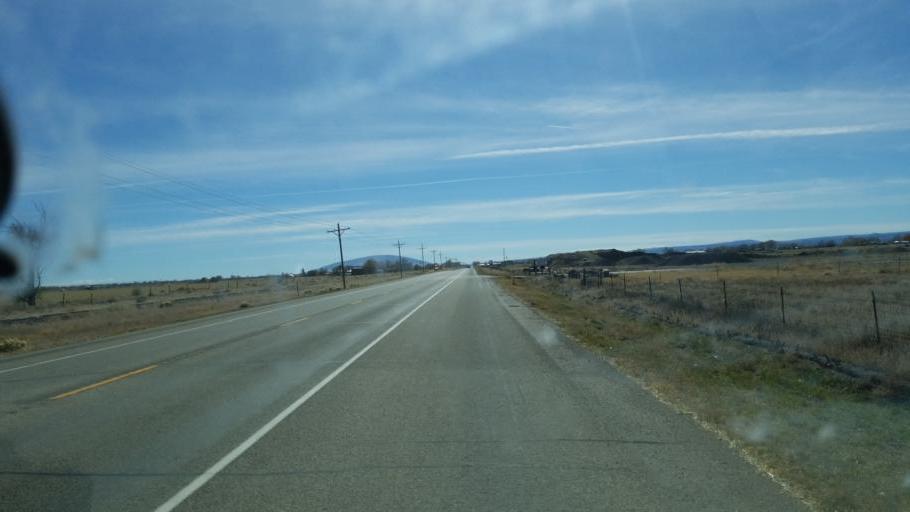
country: US
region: Colorado
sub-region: Conejos County
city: Conejos
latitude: 37.1579
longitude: -105.9922
